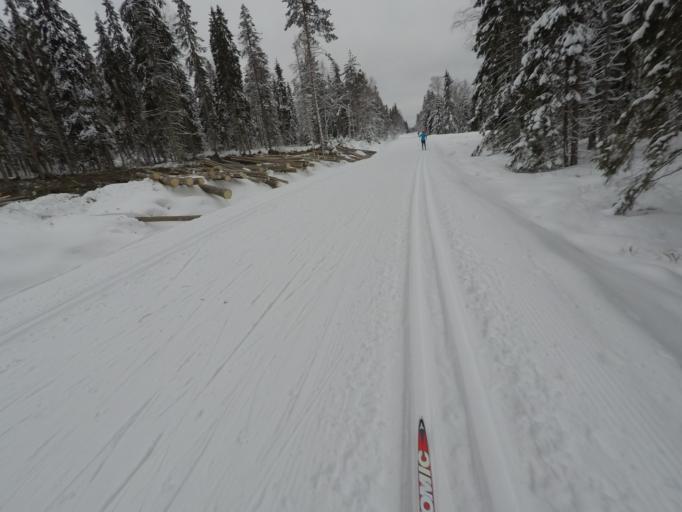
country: SE
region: Dalarna
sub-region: Ludvika Kommun
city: Abborrberget
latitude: 60.1550
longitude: 14.4896
